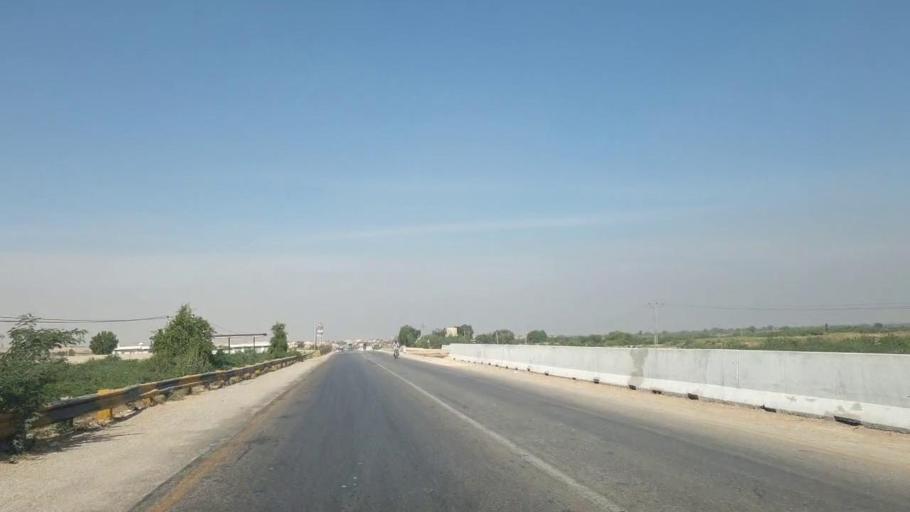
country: PK
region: Sindh
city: Hala
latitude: 25.7208
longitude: 68.2929
